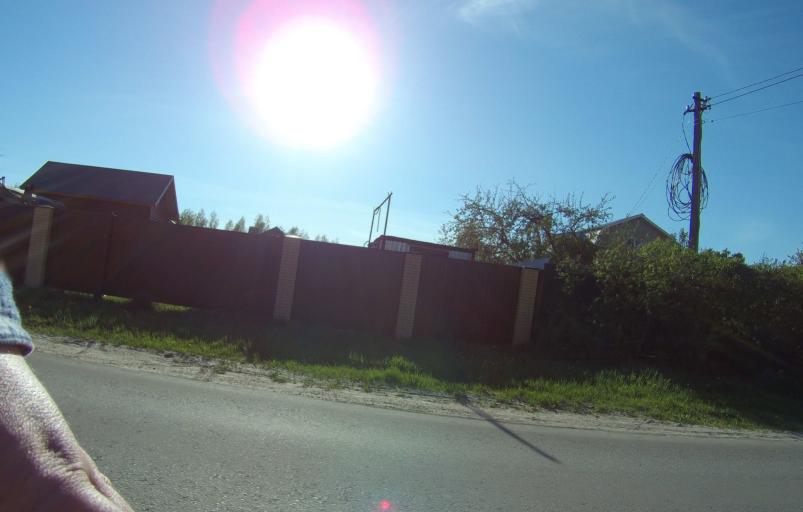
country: RU
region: Moskovskaya
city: Ramenskoye
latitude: 55.5479
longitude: 38.1961
